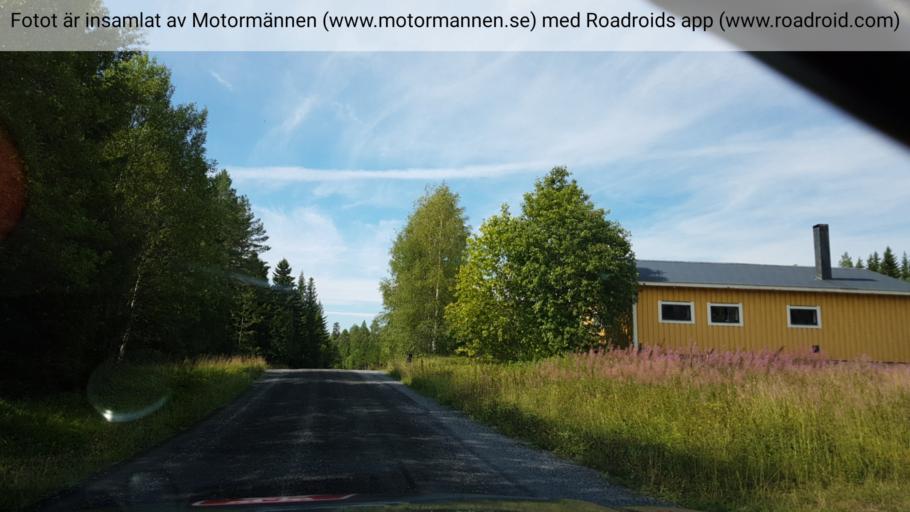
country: SE
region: Jaemtland
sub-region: Krokoms Kommun
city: Valla
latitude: 63.3051
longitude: 13.9467
